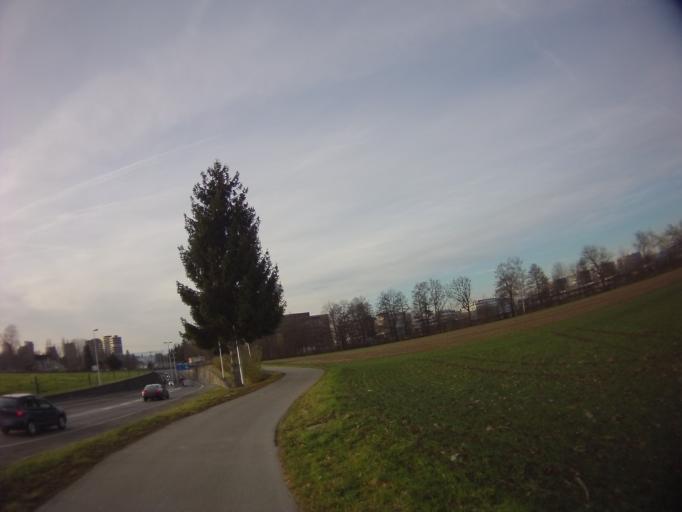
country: CH
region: Zug
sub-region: Zug
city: Steinhausen
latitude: 47.1842
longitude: 8.4824
